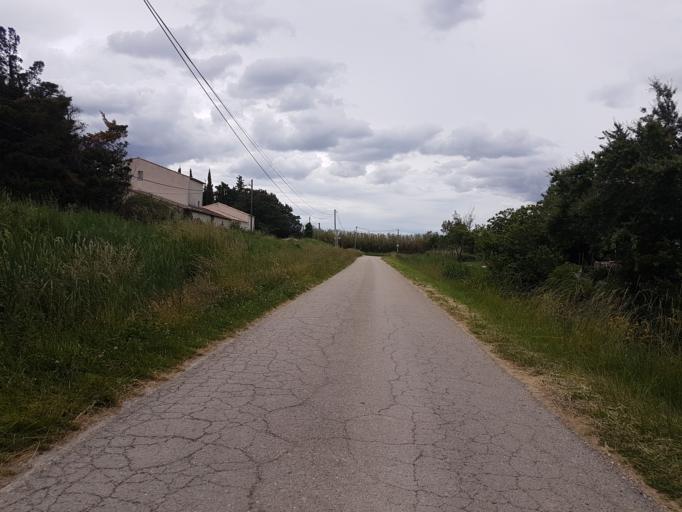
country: FR
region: Languedoc-Roussillon
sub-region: Departement du Gard
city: Fourques
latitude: 43.7131
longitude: 4.5870
